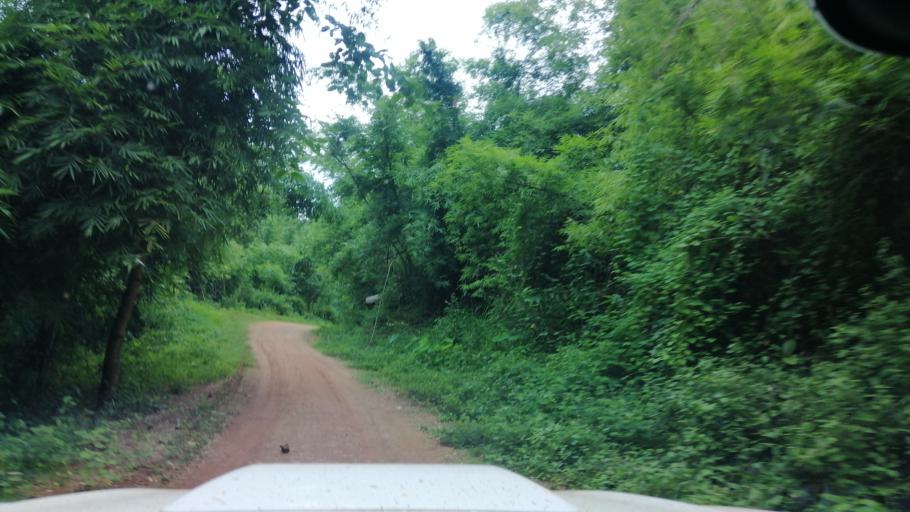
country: TH
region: Nan
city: Mae Charim
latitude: 18.7650
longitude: 101.3049
